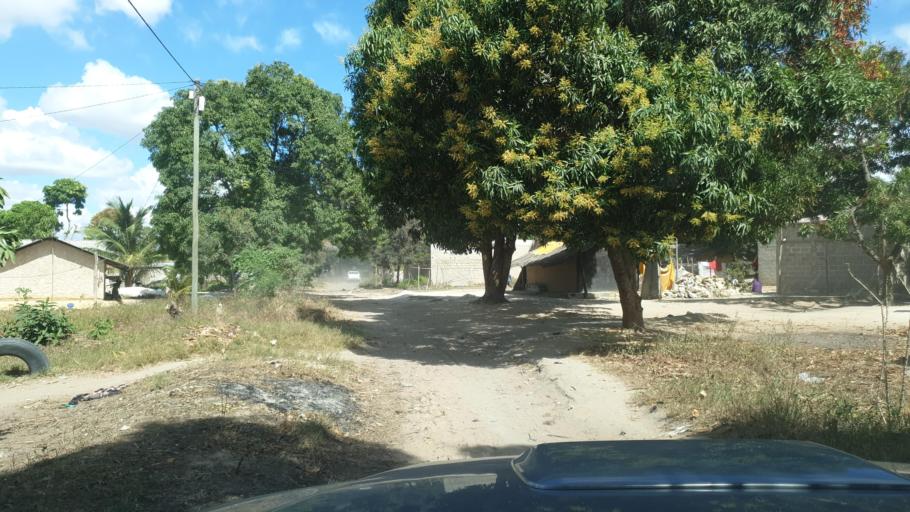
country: MZ
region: Nampula
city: Nacala
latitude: -14.5721
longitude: 40.6971
